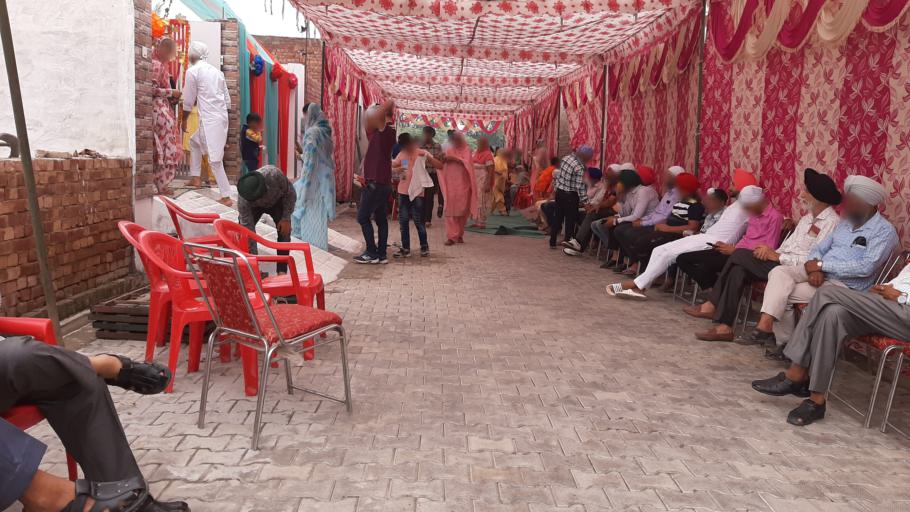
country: IN
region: Punjab
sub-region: Sangrur
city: Sunam
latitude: 30.1359
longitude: 75.8002
